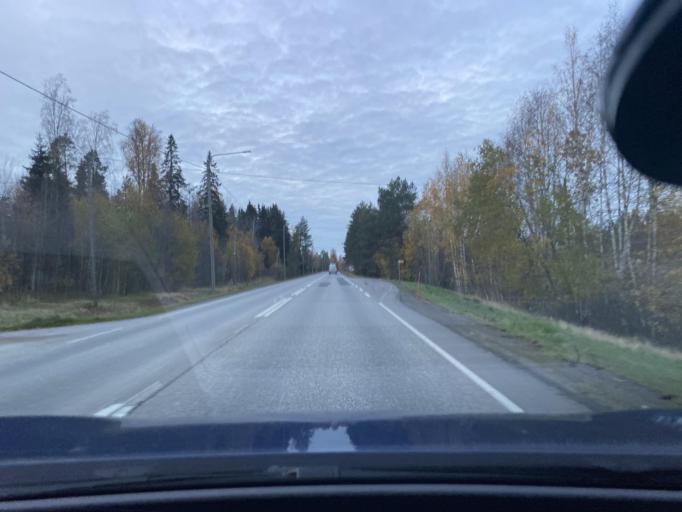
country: FI
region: Uusimaa
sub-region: Helsinki
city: Vihti
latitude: 60.3376
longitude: 24.1983
